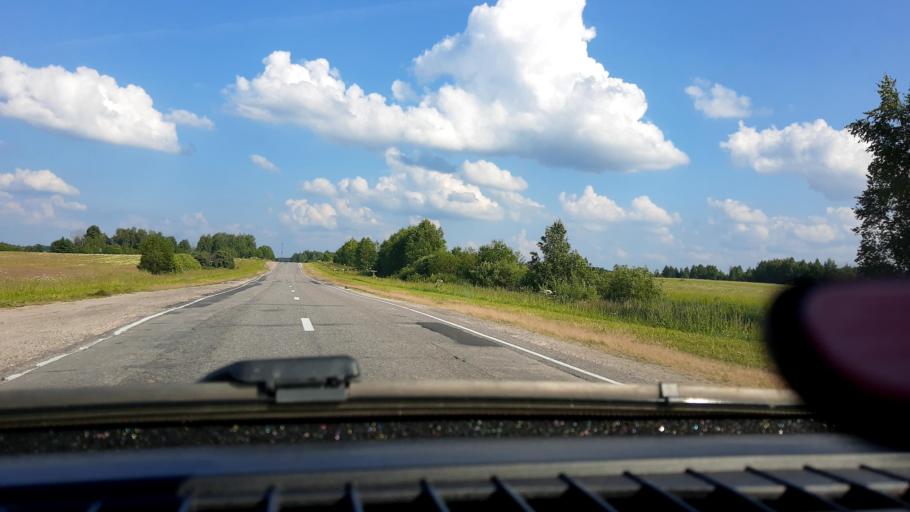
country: RU
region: Nizjnij Novgorod
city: Neklyudovo
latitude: 56.5004
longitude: 43.9914
